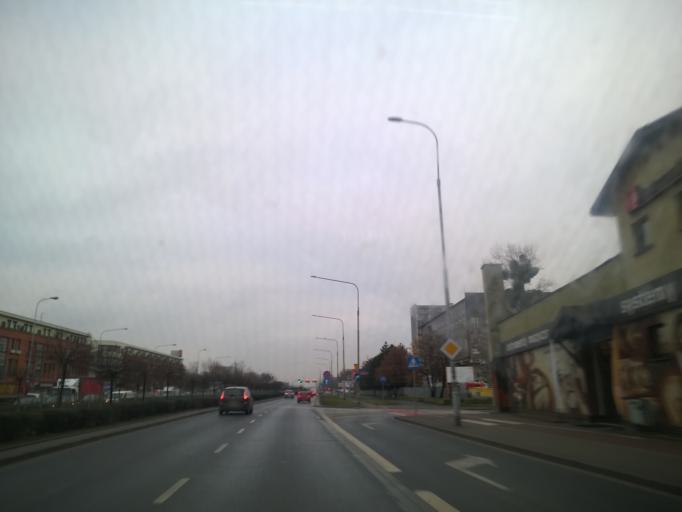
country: PL
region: Lower Silesian Voivodeship
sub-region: Powiat wroclawski
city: Wroclaw
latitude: 51.0831
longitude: 17.0372
